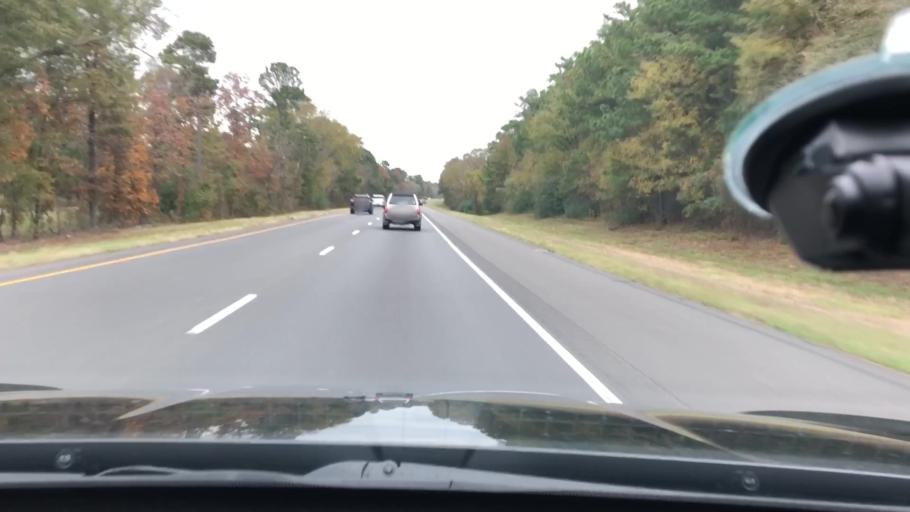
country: US
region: Arkansas
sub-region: Hempstead County
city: Hope
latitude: 33.7125
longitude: -93.5685
